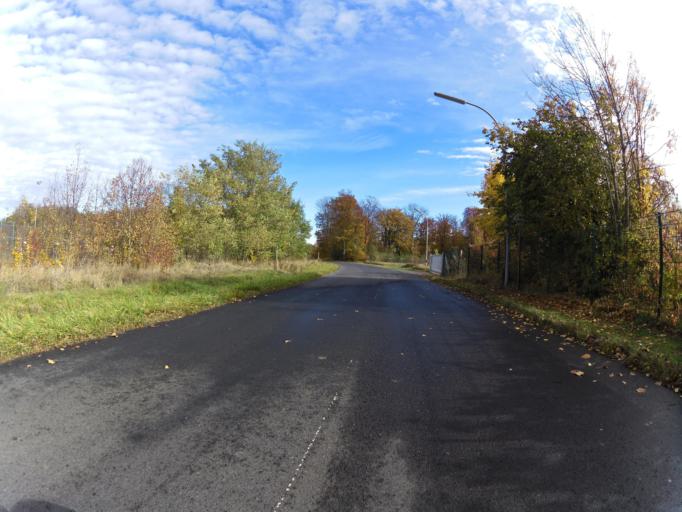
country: DE
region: Bavaria
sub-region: Regierungsbezirk Unterfranken
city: Gaukonigshofen
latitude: 49.6577
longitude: 9.9778
